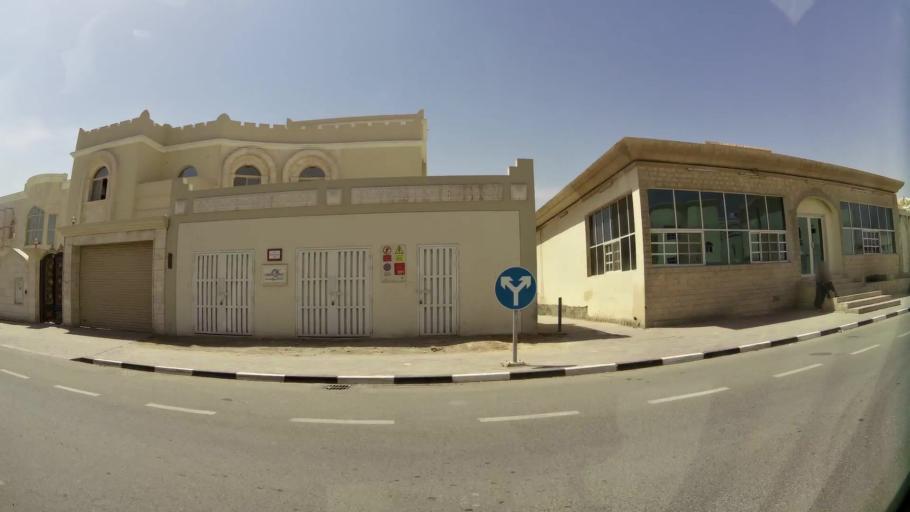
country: QA
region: Baladiyat ar Rayyan
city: Ar Rayyan
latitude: 25.2813
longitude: 51.4078
